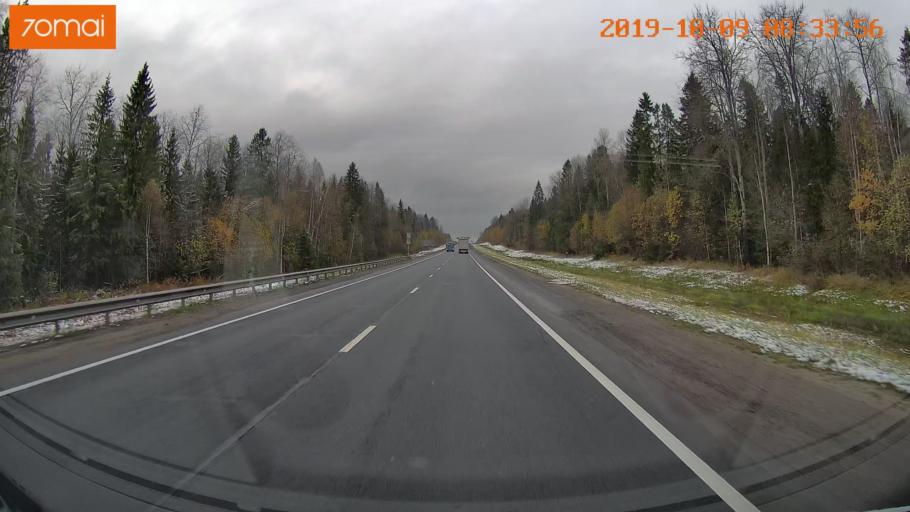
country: RU
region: Vologda
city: Gryazovets
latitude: 58.8895
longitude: 40.1889
